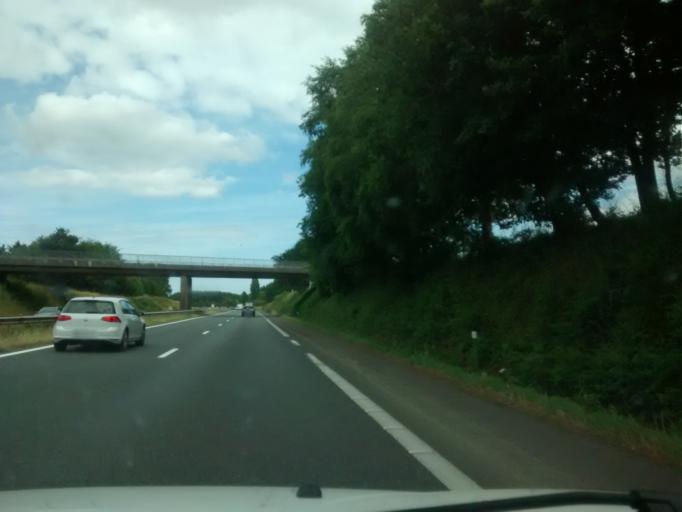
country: FR
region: Brittany
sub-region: Departement des Cotes-d'Armor
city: Lanrodec
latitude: 48.5356
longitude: -3.0455
